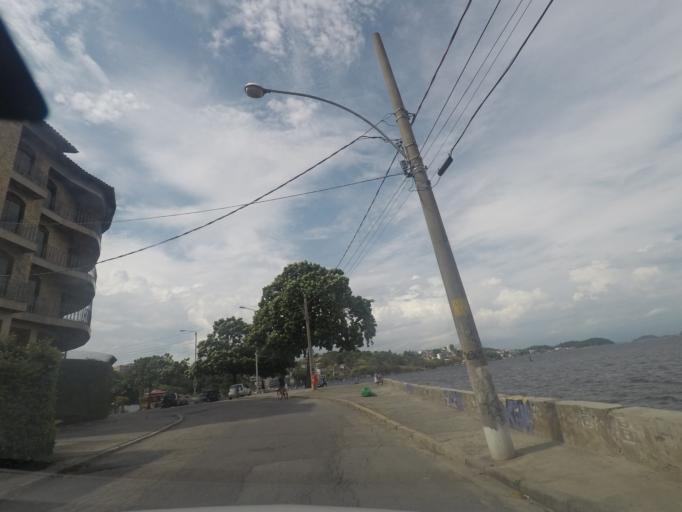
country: BR
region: Rio de Janeiro
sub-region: Rio De Janeiro
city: Rio de Janeiro
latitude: -22.8064
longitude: -43.1776
